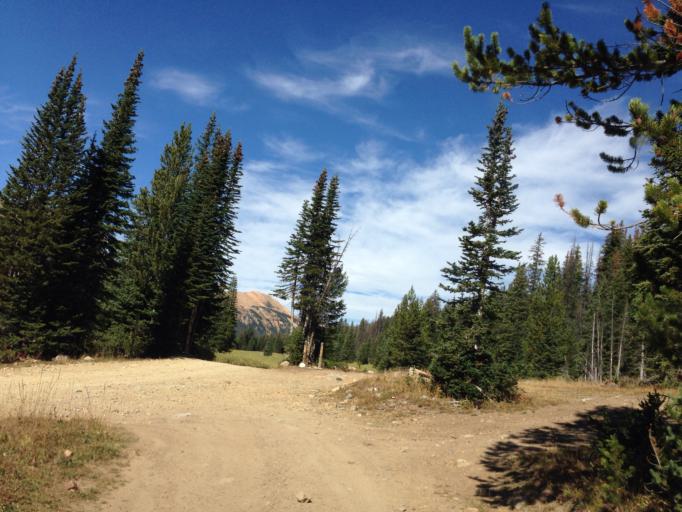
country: US
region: Montana
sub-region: Stillwater County
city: Absarokee
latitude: 45.0518
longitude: -109.9147
